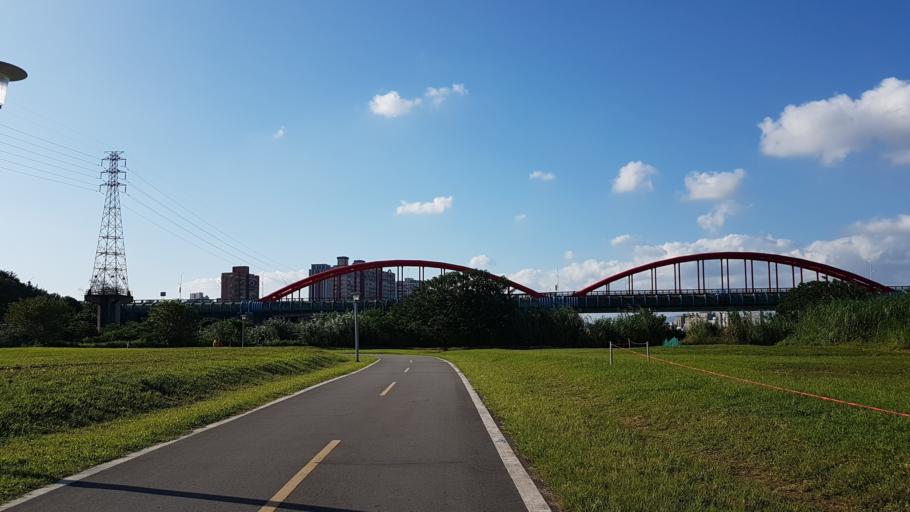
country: TW
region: Taipei
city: Taipei
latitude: 25.0089
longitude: 121.5281
